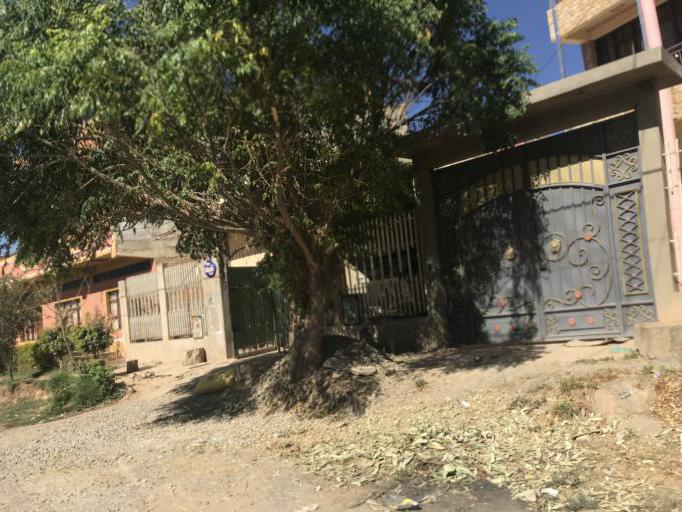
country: BO
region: Cochabamba
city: Cliza
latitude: -17.5864
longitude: -65.9200
